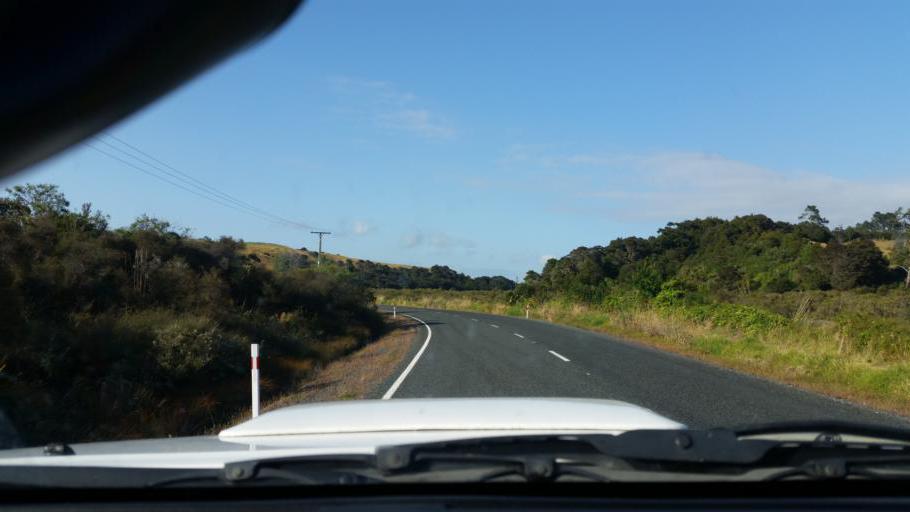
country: NZ
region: Northland
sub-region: Whangarei
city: Ruakaka
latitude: -36.1126
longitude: 174.2297
